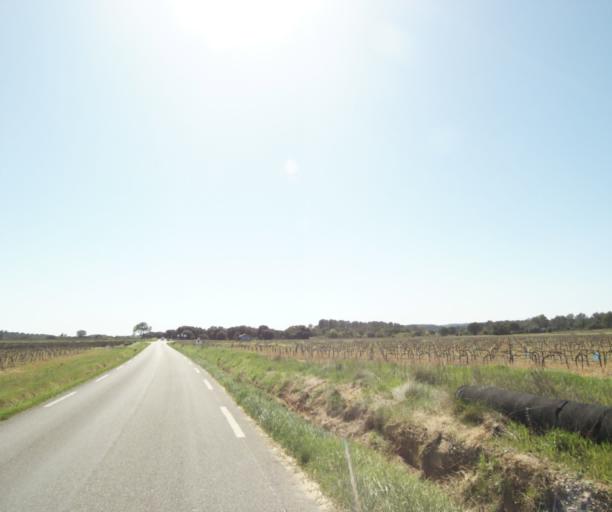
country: FR
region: Languedoc-Roussillon
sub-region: Departement de l'Herault
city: Beaulieu
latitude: 43.7342
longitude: 4.0099
